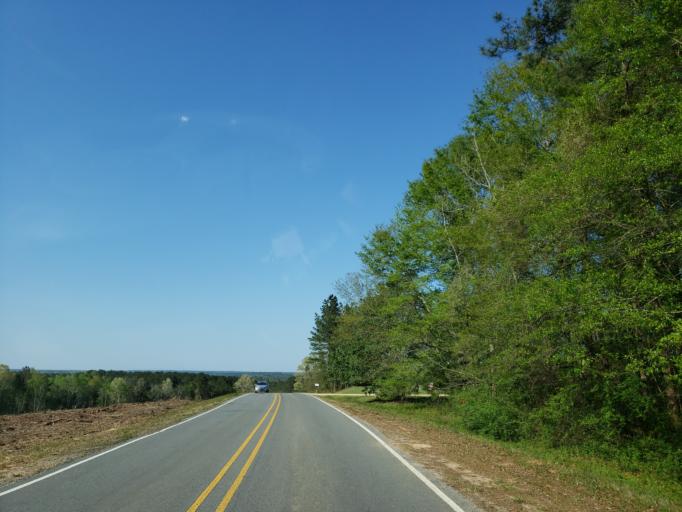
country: US
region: Mississippi
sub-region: Covington County
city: Collins
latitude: 31.6791
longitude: -89.4147
